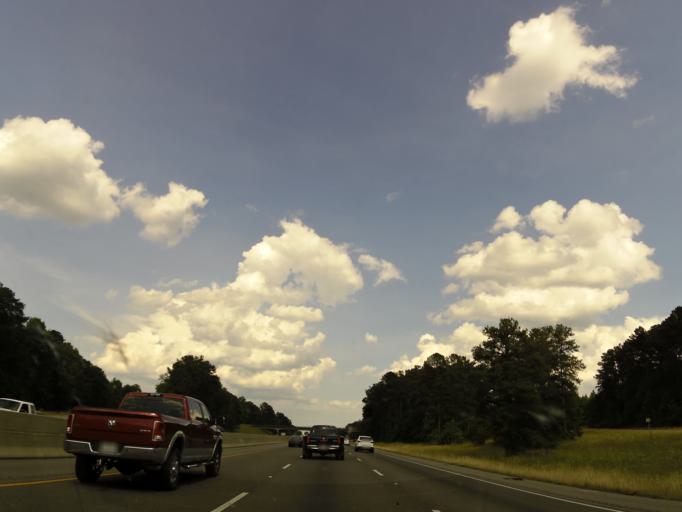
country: US
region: Alabama
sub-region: Tuscaloosa County
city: Coaling
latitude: 33.1891
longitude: -87.3049
